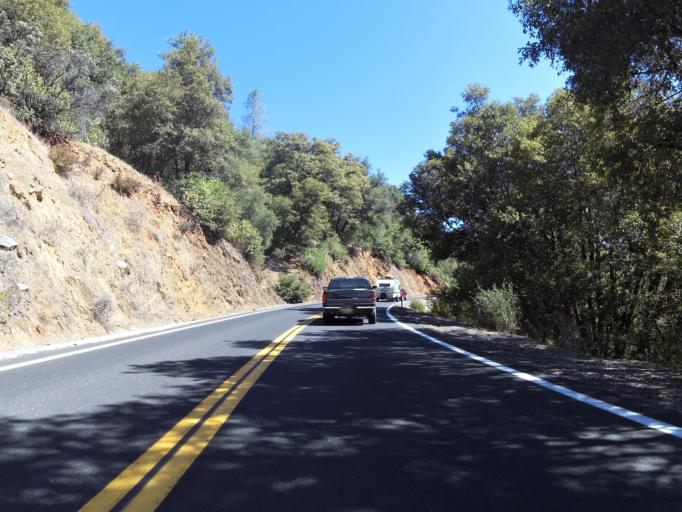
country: US
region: California
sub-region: Calaveras County
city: Murphys
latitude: 38.1485
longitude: -120.4462
